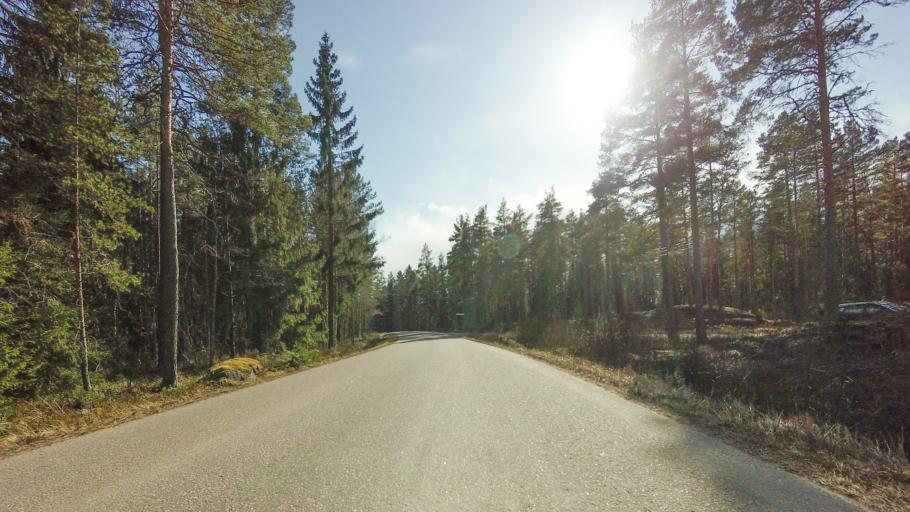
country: FI
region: Varsinais-Suomi
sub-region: Salo
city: Suomusjaervi
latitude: 60.3353
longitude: 23.6495
